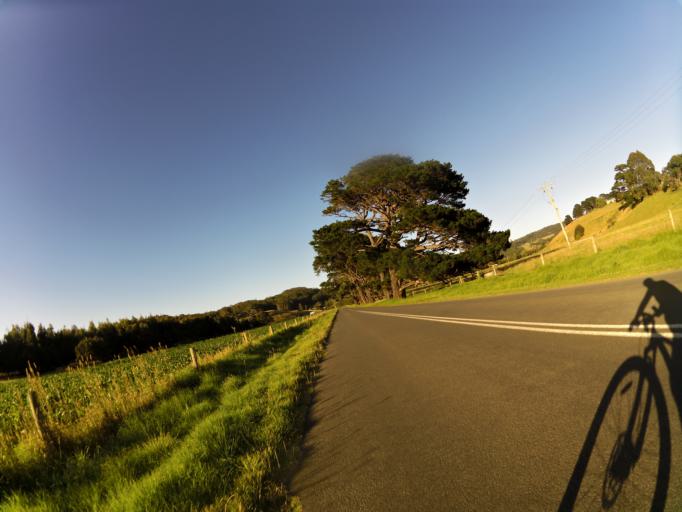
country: AU
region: Victoria
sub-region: Colac-Otway
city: Apollo Bay
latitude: -38.7679
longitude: 143.6522
